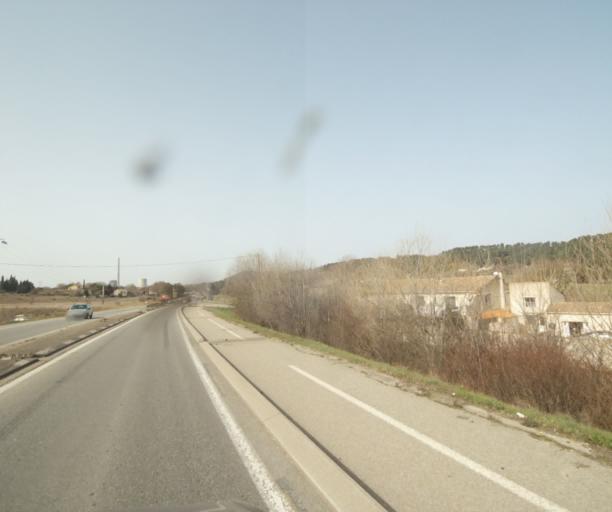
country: FR
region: Provence-Alpes-Cote d'Azur
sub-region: Departement des Bouches-du-Rhone
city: Meyreuil
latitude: 43.4754
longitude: 5.5276
